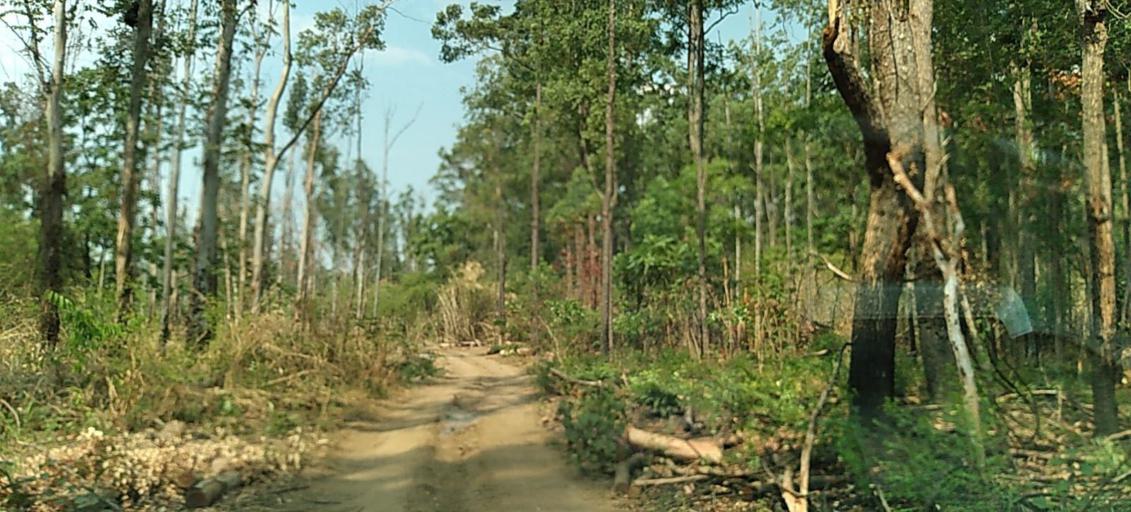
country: ZM
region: Copperbelt
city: Chingola
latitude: -12.7387
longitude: 27.7546
